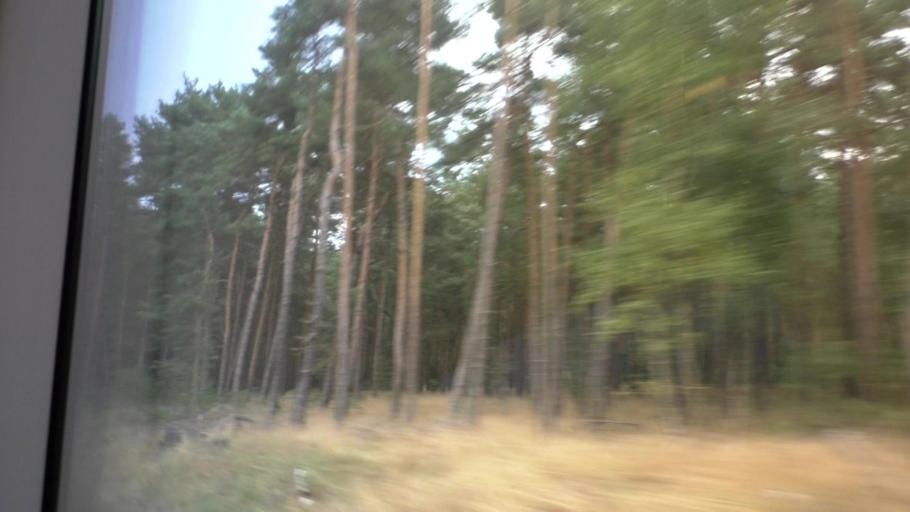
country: DE
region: Brandenburg
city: Mullrose
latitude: 52.2197
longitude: 14.4263
